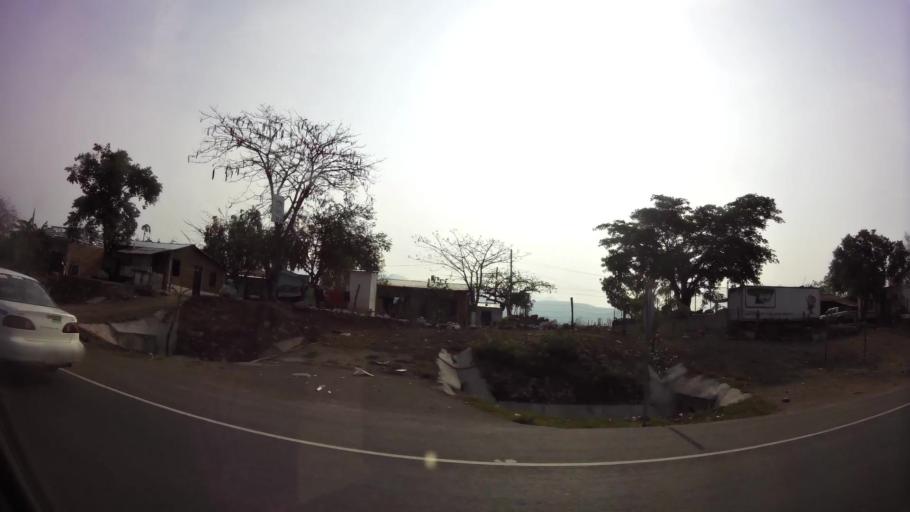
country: HN
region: Comayagua
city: Comayagua
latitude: 14.3985
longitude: -87.6171
